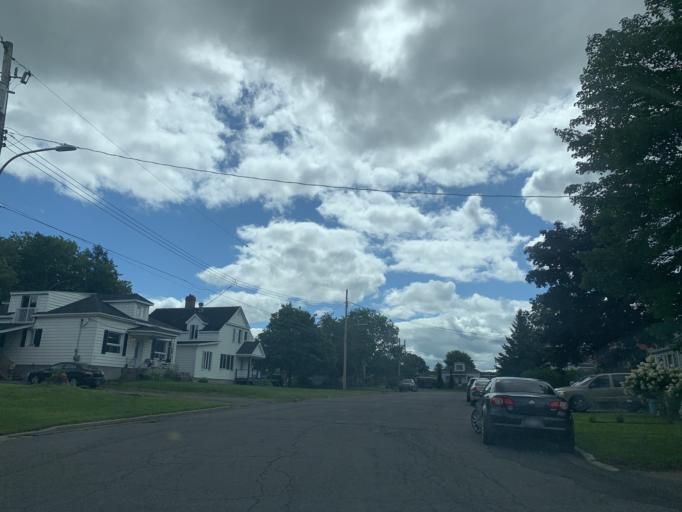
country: CA
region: Ontario
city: Hawkesbury
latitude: 45.6055
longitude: -74.6043
